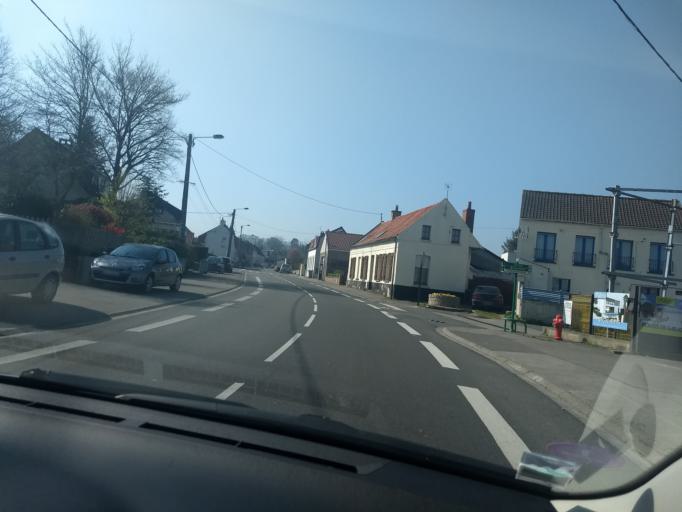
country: FR
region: Nord-Pas-de-Calais
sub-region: Departement du Pas-de-Calais
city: Tatinghem
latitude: 50.7482
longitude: 2.2146
